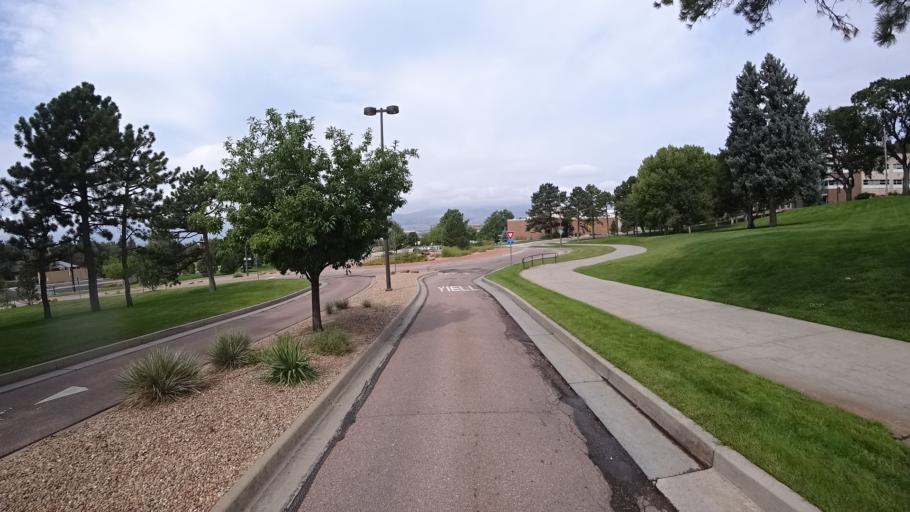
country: US
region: Colorado
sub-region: El Paso County
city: Colorado Springs
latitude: 38.8913
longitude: -104.7972
